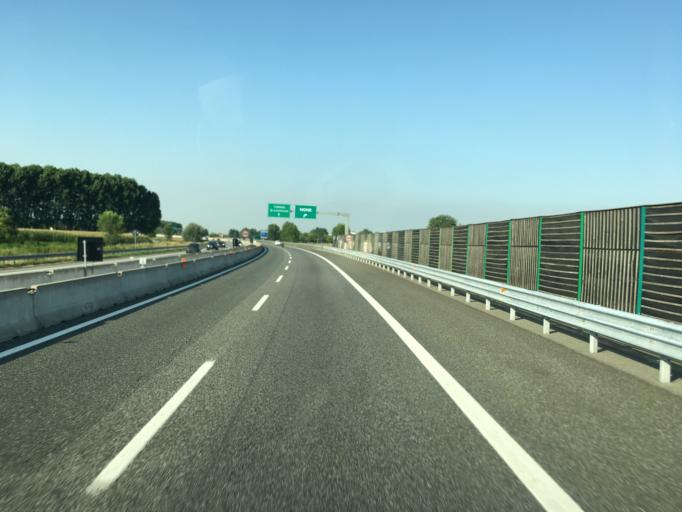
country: IT
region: Piedmont
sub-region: Provincia di Torino
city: Volvera
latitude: 44.9339
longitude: 7.5002
